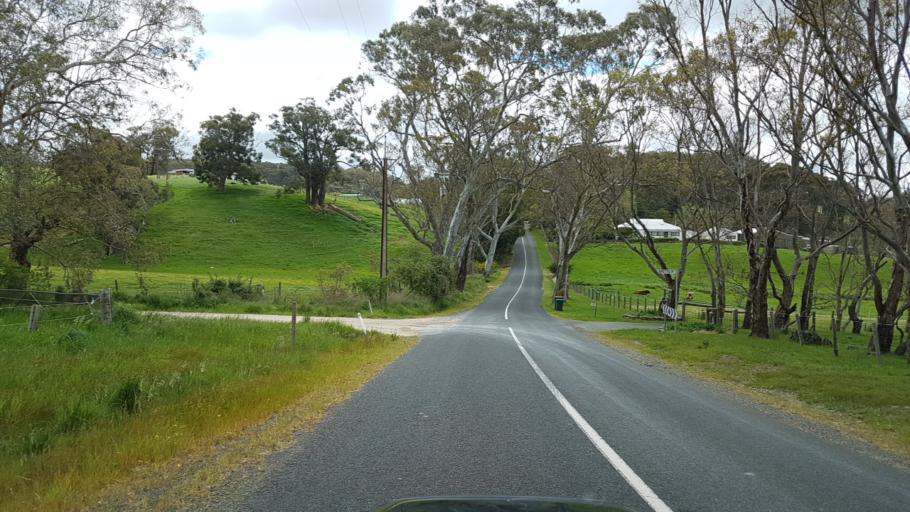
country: AU
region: South Australia
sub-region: Adelaide Hills
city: Lobethal
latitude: -34.8888
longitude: 138.8904
